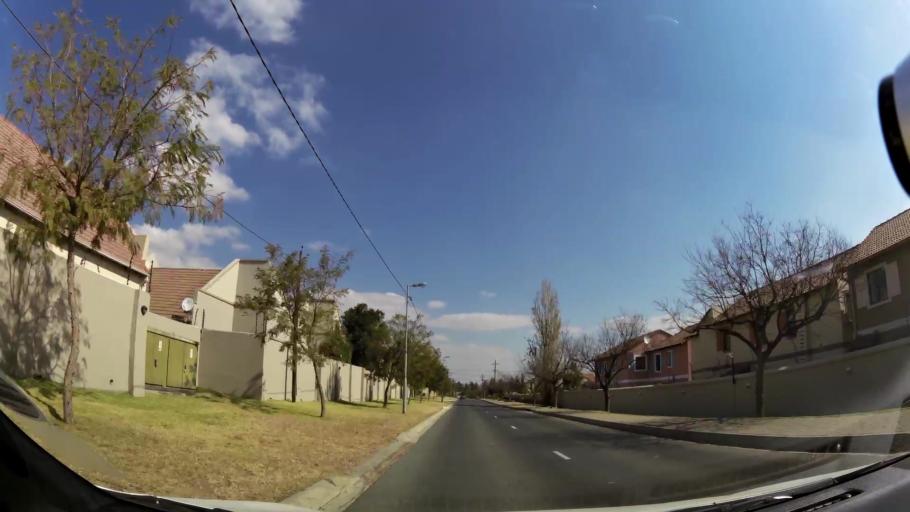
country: ZA
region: Gauteng
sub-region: City of Johannesburg Metropolitan Municipality
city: Midrand
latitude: -26.0123
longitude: 28.0737
